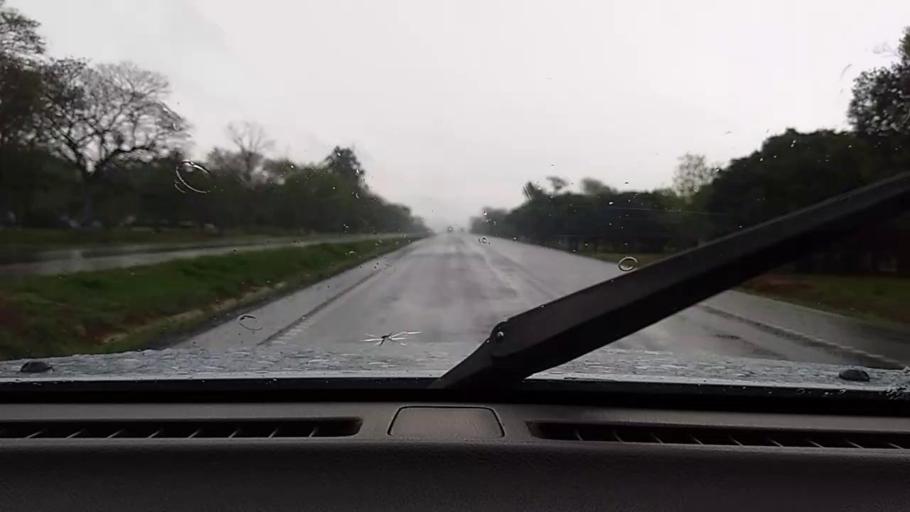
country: PY
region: Caaguazu
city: Repatriacion
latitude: -25.4514
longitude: -55.9023
